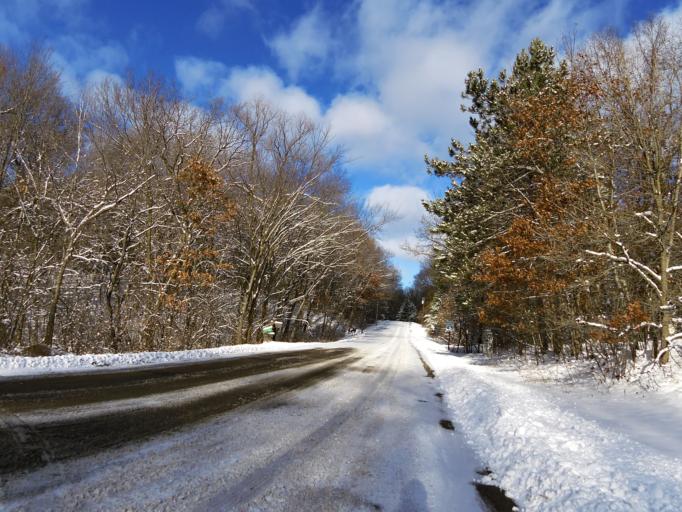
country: US
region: Minnesota
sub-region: Washington County
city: Lake Elmo
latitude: 44.9642
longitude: -92.8369
